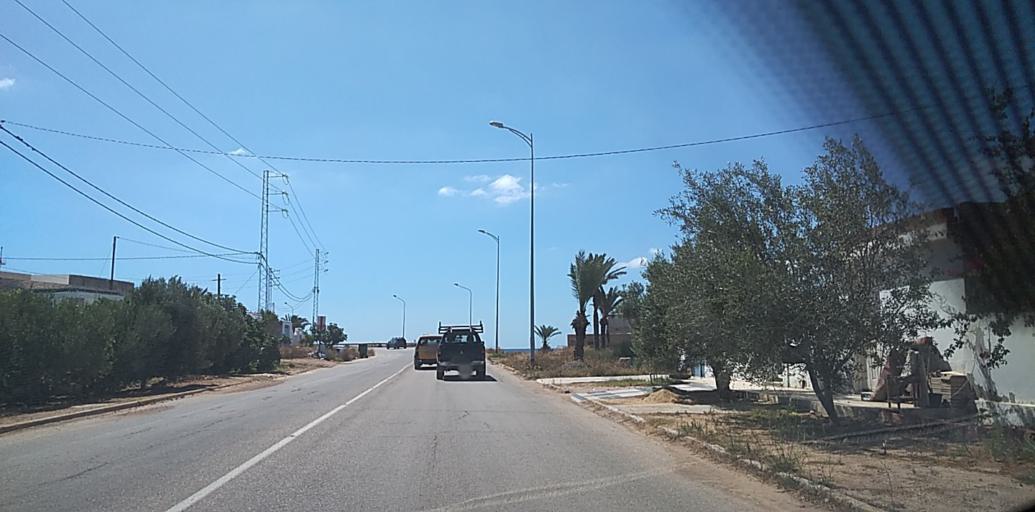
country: TN
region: Safaqis
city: Al Qarmadah
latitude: 34.6729
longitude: 11.1414
